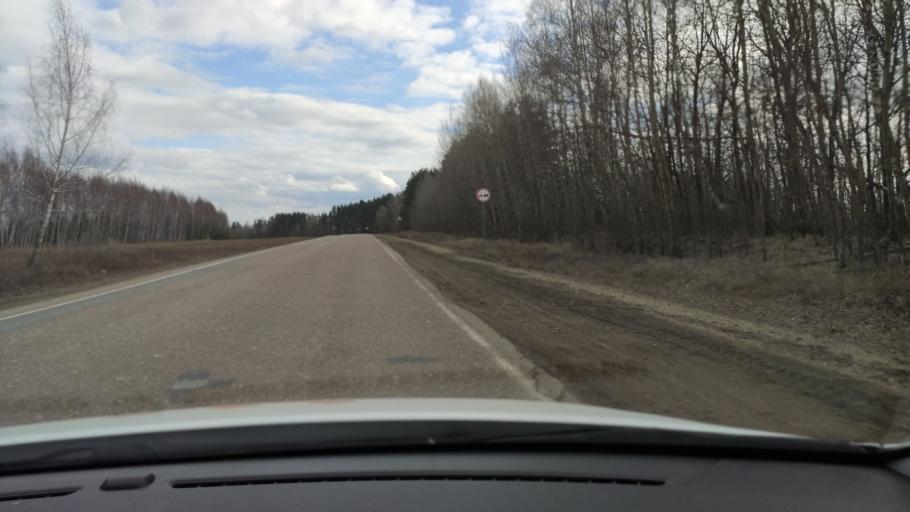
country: RU
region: Tatarstan
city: Vysokaya Gora
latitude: 56.0703
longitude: 49.1941
